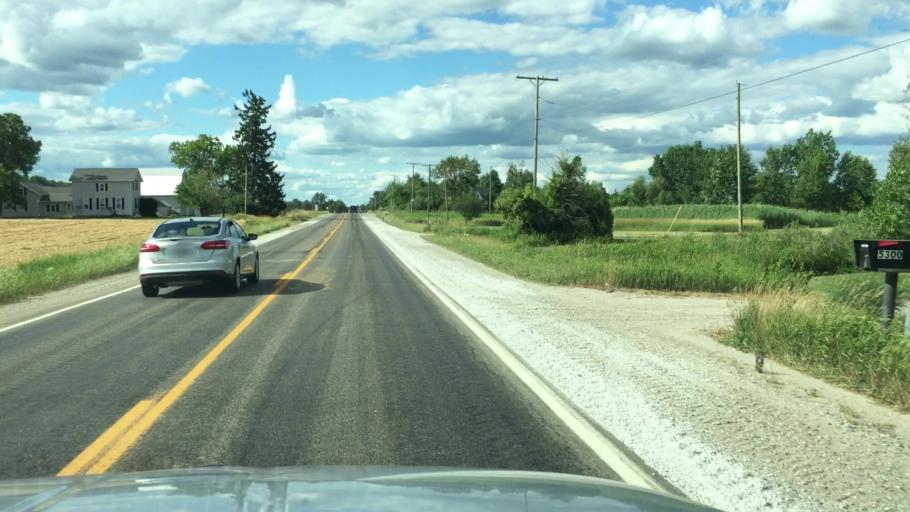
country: US
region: Michigan
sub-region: Saint Clair County
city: Capac
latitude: 43.0492
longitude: -82.9295
